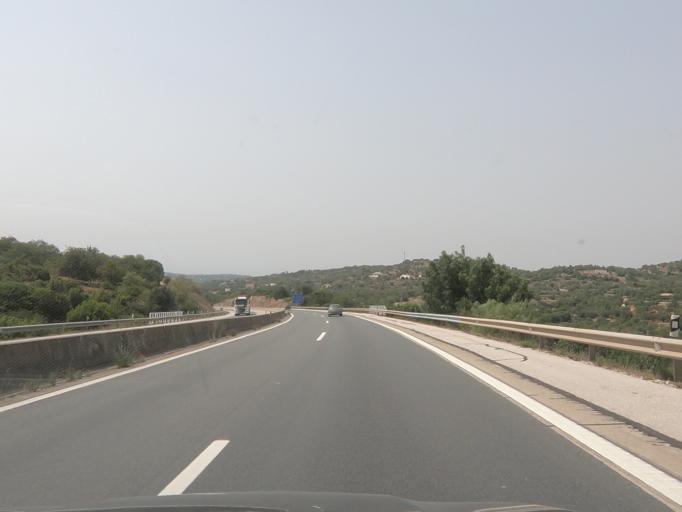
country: PT
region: Faro
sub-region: Loule
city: Boliqueime
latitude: 37.1583
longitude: -8.1812
